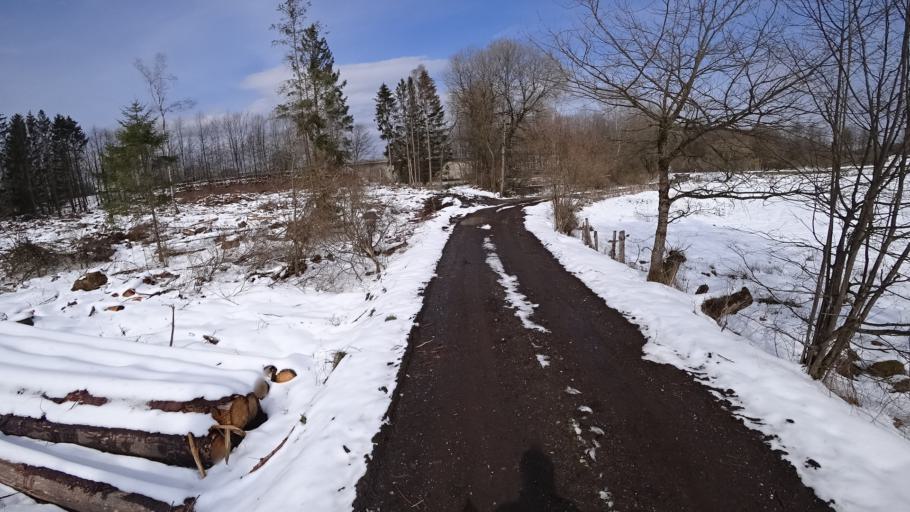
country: DE
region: Rheinland-Pfalz
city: Kausen
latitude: 50.7216
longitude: 7.8705
